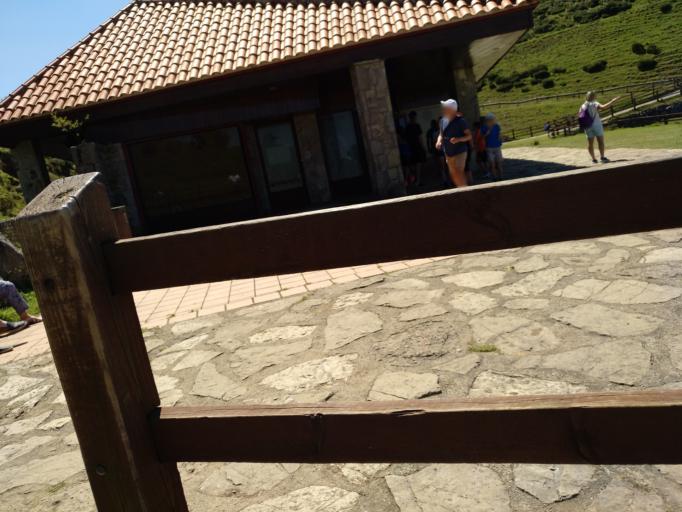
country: ES
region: Asturias
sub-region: Province of Asturias
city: Amieva
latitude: 43.2772
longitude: -4.9833
